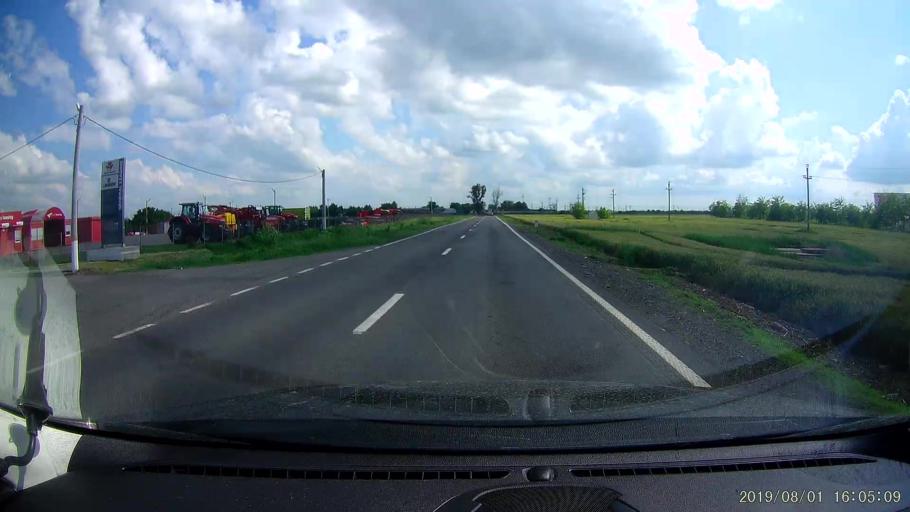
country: RO
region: Calarasi
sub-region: Comuna Dragalina
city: Drajna Noua
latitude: 44.4311
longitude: 27.3772
